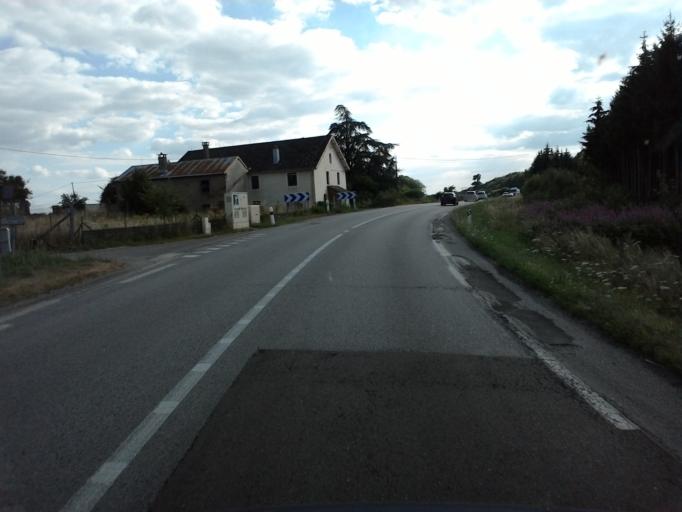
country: FR
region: Franche-Comte
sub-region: Departement de la Haute-Saone
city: Fougerolles
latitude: 47.9242
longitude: 6.4257
